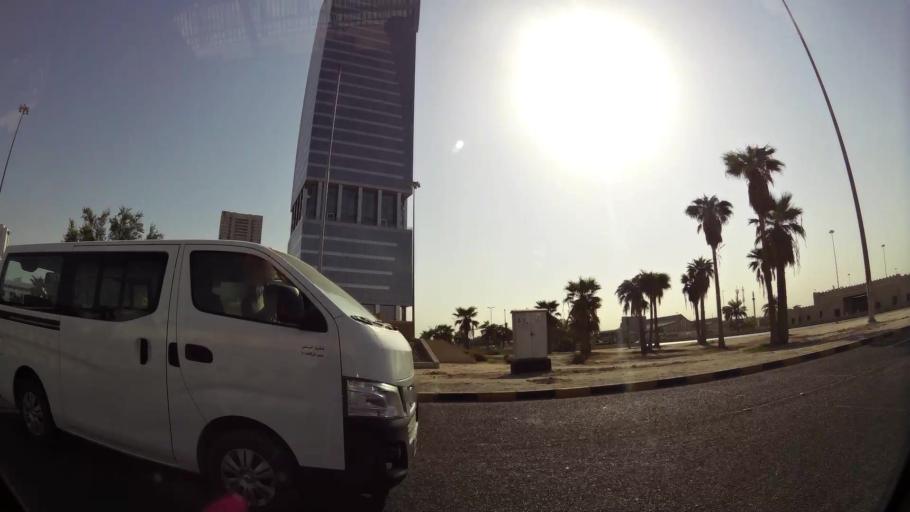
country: KW
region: Al Asimah
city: Kuwait City
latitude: 29.3624
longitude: 47.9740
